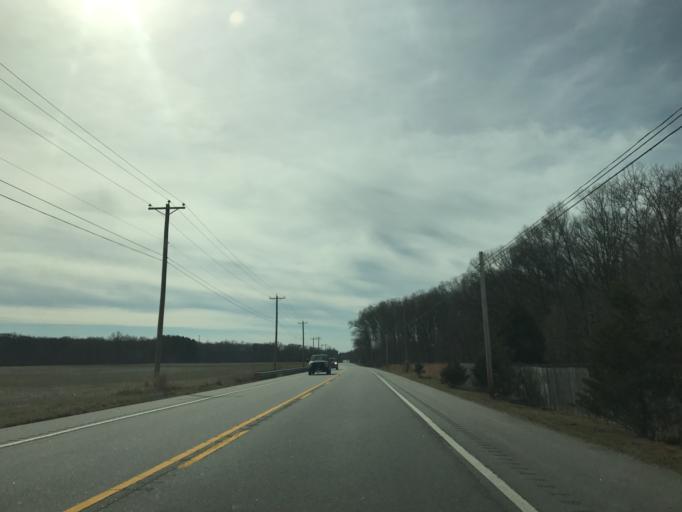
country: US
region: Maryland
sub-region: Queen Anne's County
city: Kingstown
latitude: 39.1287
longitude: -76.0036
